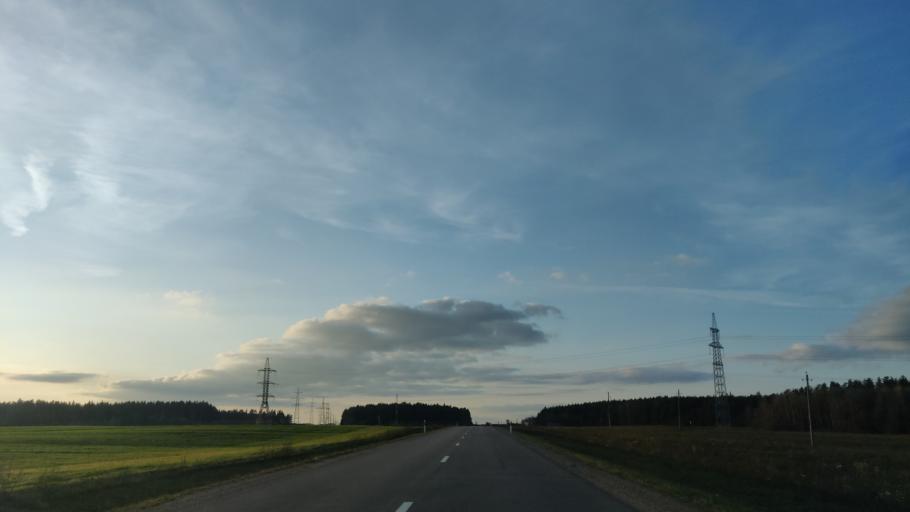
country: LT
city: Lentvaris
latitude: 54.5950
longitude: 25.0382
